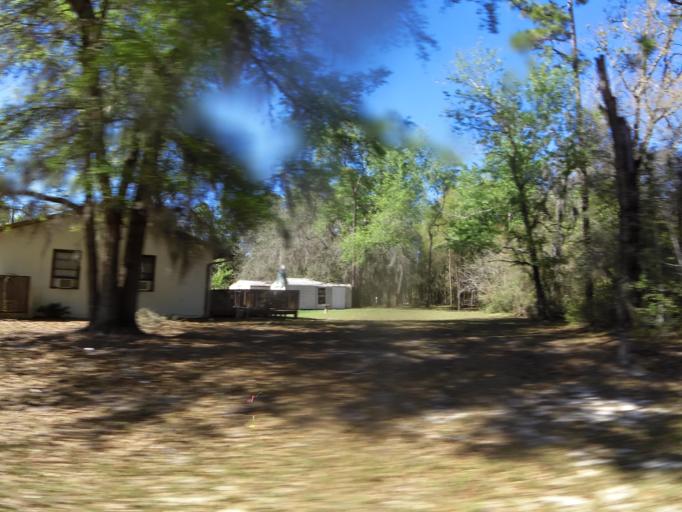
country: US
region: Florida
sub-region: Clay County
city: Keystone Heights
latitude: 29.8000
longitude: -82.0513
